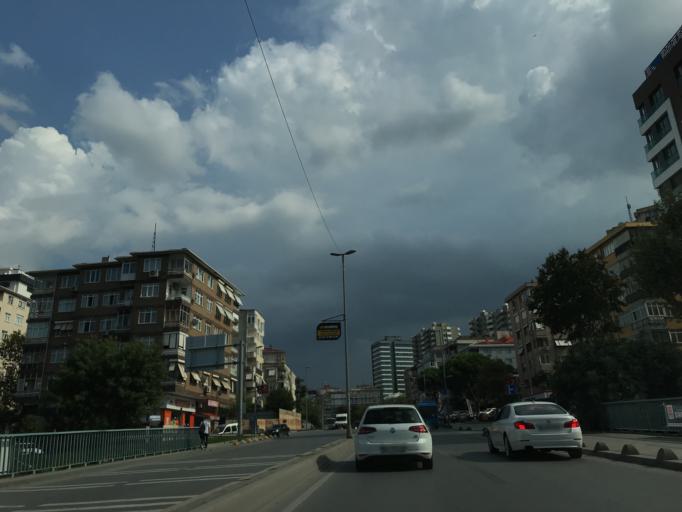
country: TR
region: Istanbul
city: UEskuedar
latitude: 40.9906
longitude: 29.0402
